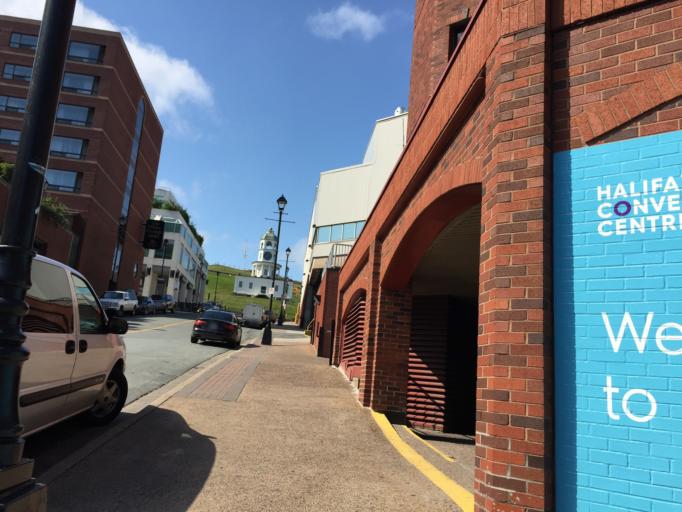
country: CA
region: Nova Scotia
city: Halifax
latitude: 44.6480
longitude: -63.5757
